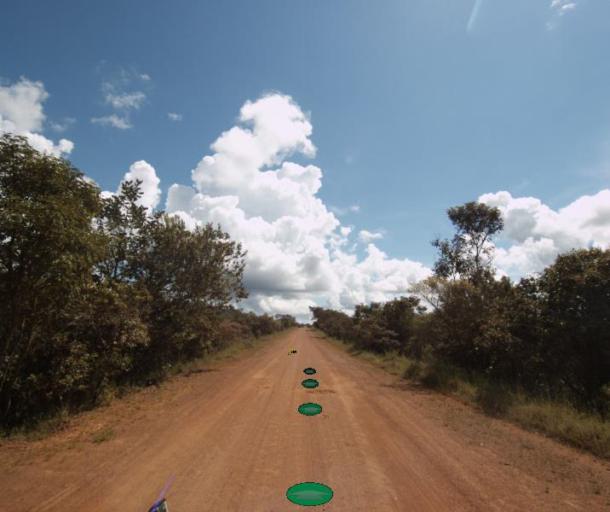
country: BR
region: Goias
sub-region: Pirenopolis
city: Pirenopolis
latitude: -15.7810
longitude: -48.8222
